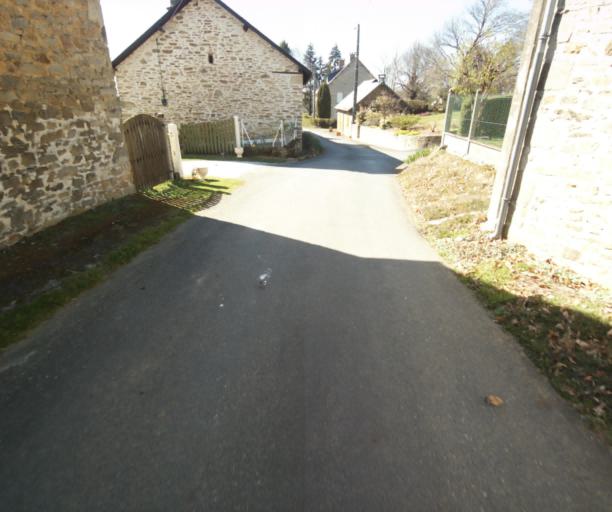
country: FR
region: Limousin
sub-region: Departement de la Correze
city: Chamboulive
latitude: 45.4714
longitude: 1.7378
